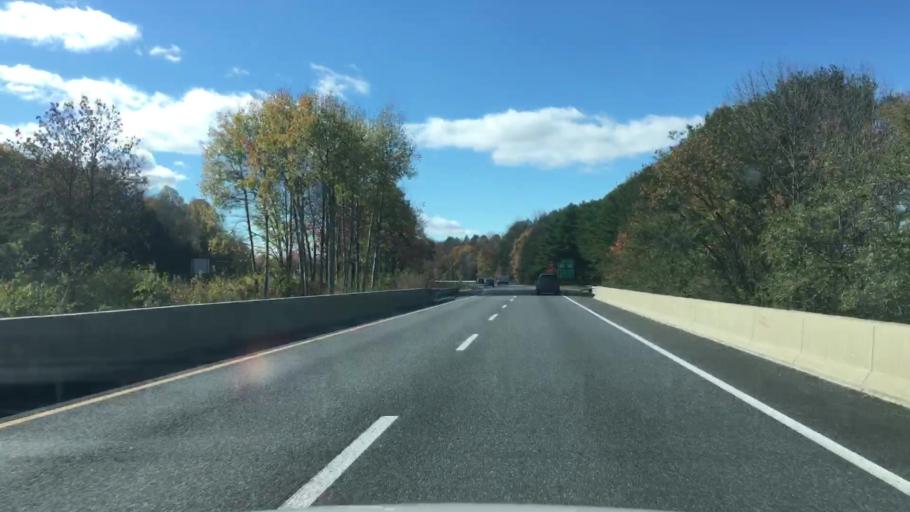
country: US
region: Maine
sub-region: Kennebec County
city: Waterville
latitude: 44.5717
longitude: -69.6563
